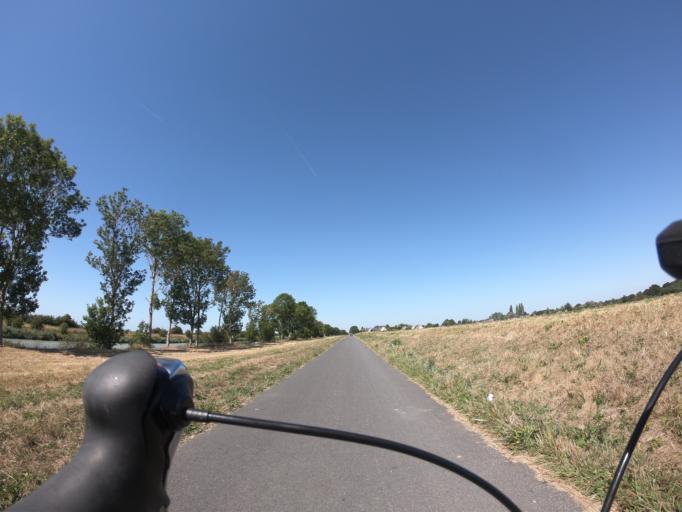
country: FR
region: Lower Normandy
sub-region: Departement de la Manche
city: Pontorson
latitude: 48.5903
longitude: -1.5151
